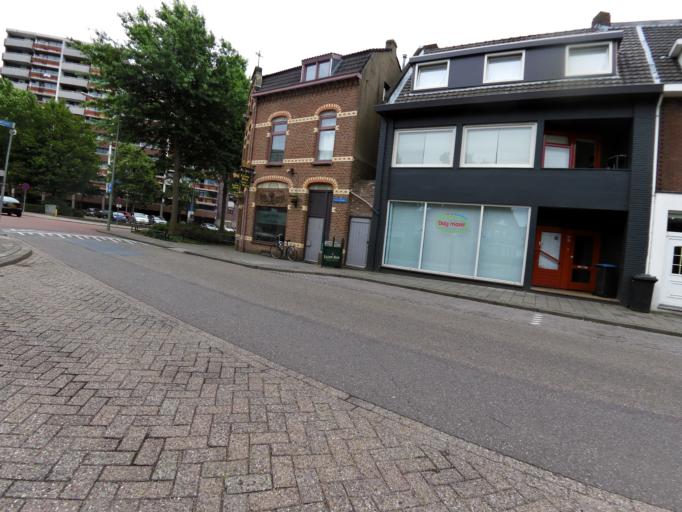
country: NL
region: Limburg
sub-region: Gemeente Heerlen
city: Heerlen
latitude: 50.8900
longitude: 5.9693
